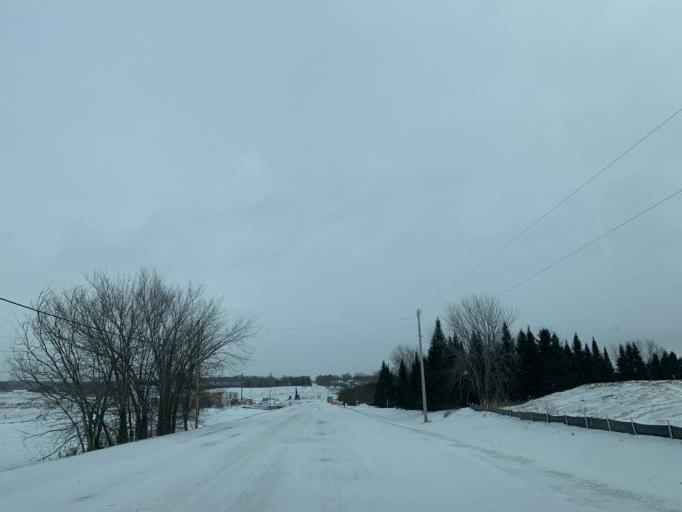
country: US
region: Minnesota
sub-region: Washington County
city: Cottage Grove
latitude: 44.8576
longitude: -92.9172
